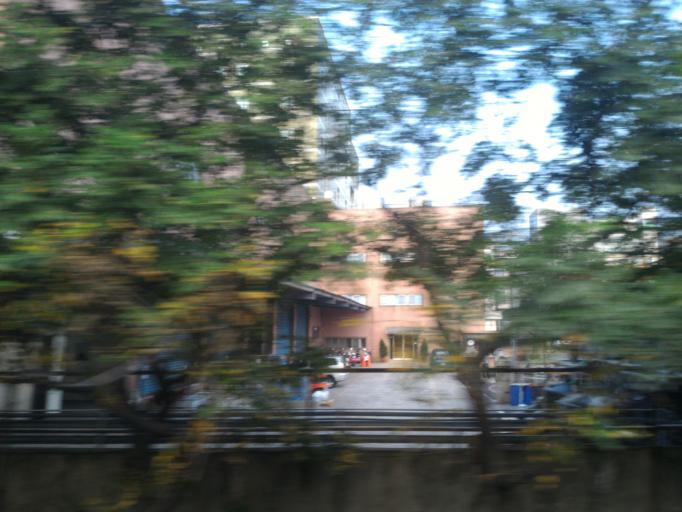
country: TW
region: Taiwan
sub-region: Taoyuan
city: Taoyuan
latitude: 24.9825
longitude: 121.3275
